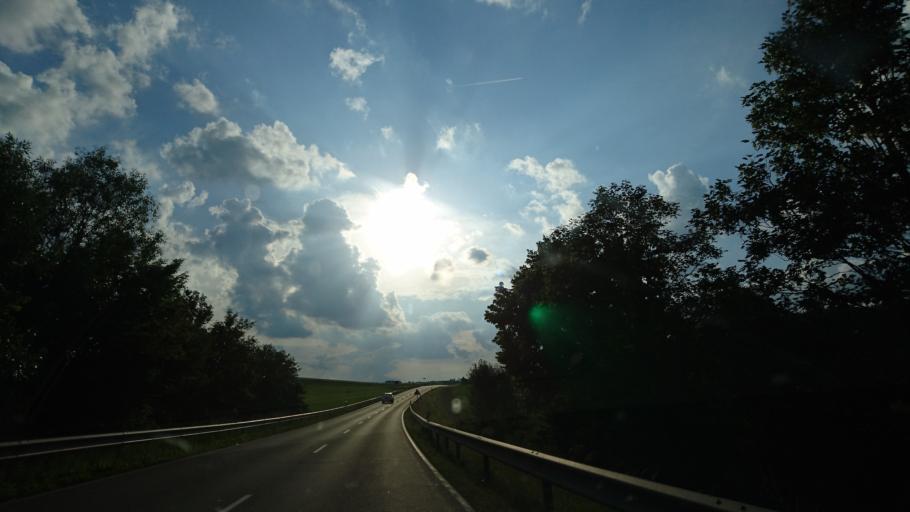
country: DE
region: Bavaria
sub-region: Lower Bavaria
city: Grafenau
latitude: 48.8756
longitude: 13.4063
